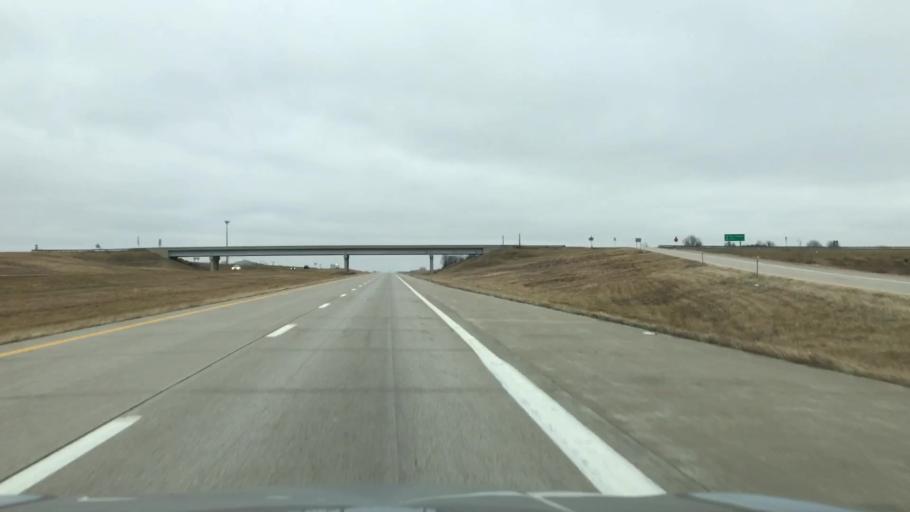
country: US
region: Missouri
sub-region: Linn County
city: Marceline
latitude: 39.7651
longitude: -92.7519
